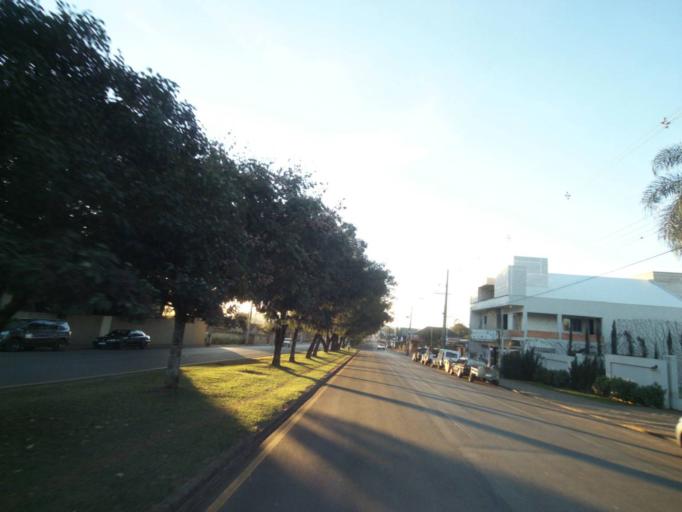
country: BR
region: Parana
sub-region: Tibagi
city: Tibagi
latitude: -24.5190
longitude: -50.4125
